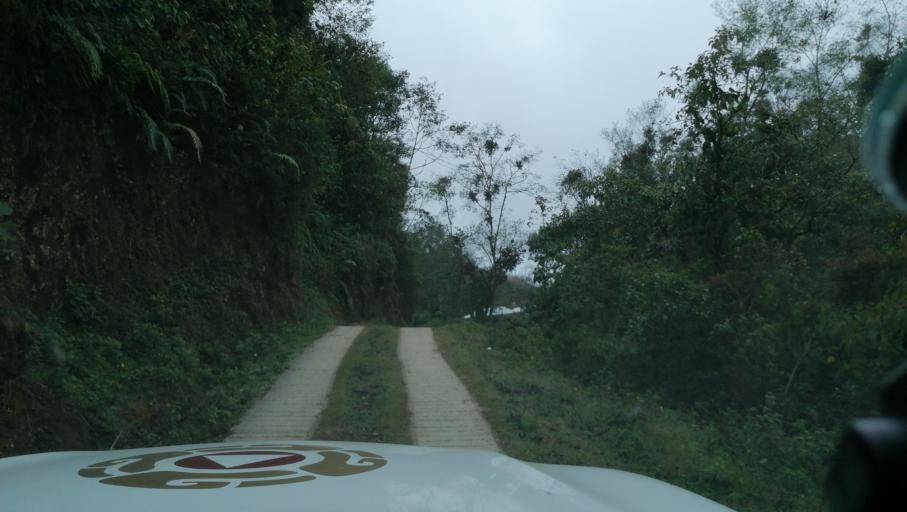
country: MX
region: Chiapas
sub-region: Cacahoatan
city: Benito Juarez
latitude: 15.1980
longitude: -92.2272
